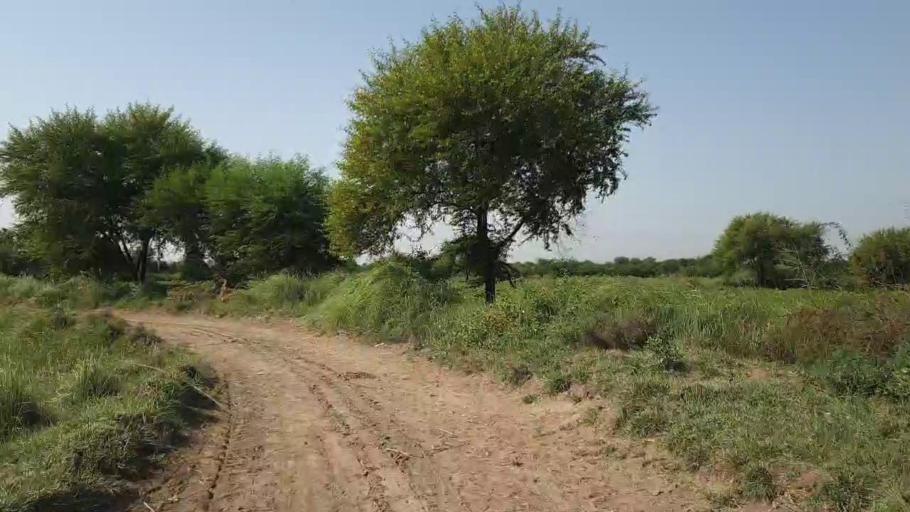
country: PK
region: Sindh
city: Kadhan
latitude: 24.6169
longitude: 69.0707
